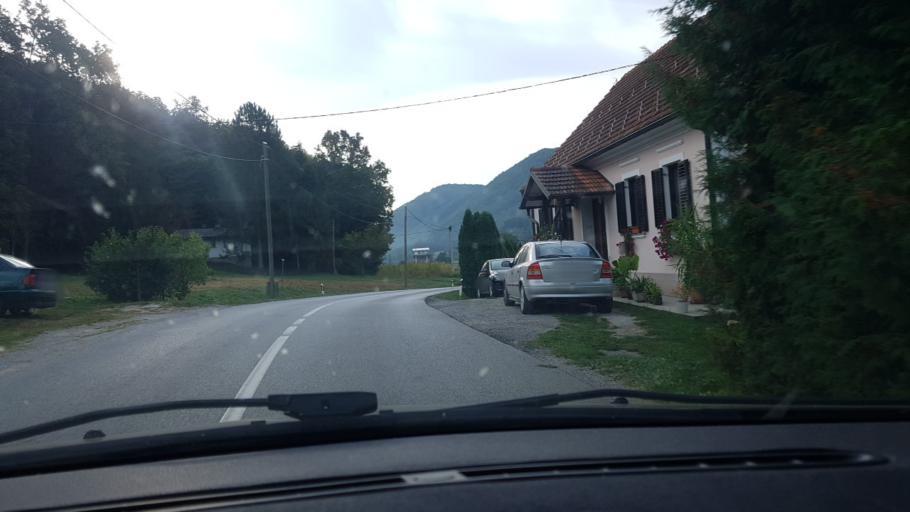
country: HR
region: Krapinsko-Zagorska
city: Mihovljan
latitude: 46.1260
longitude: 15.9805
